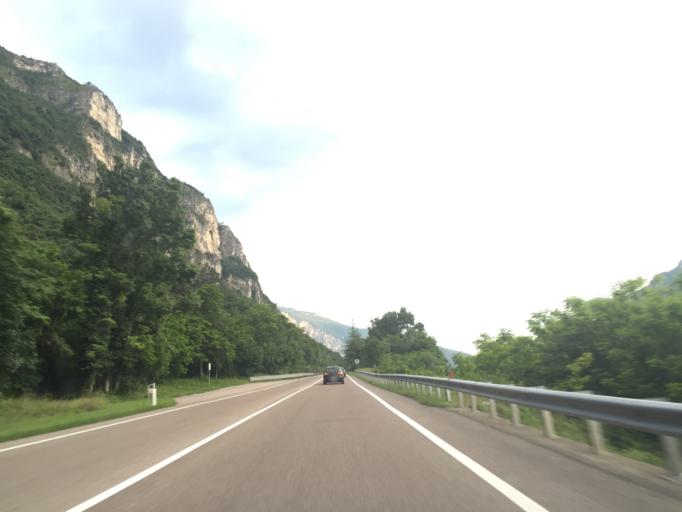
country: IT
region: Trentino-Alto Adige
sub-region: Provincia di Trento
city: Aldeno
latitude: 45.9681
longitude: 11.1129
